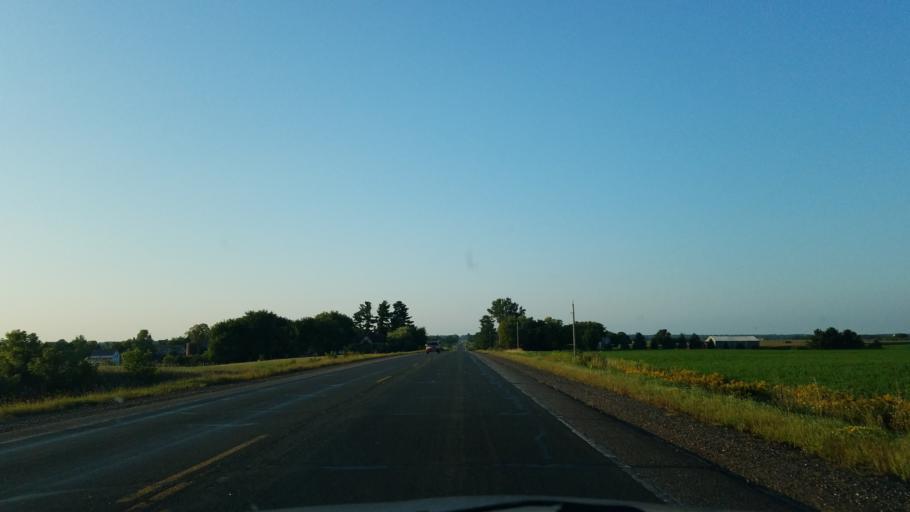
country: US
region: Wisconsin
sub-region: Polk County
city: Clear Lake
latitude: 45.2135
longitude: -92.2841
